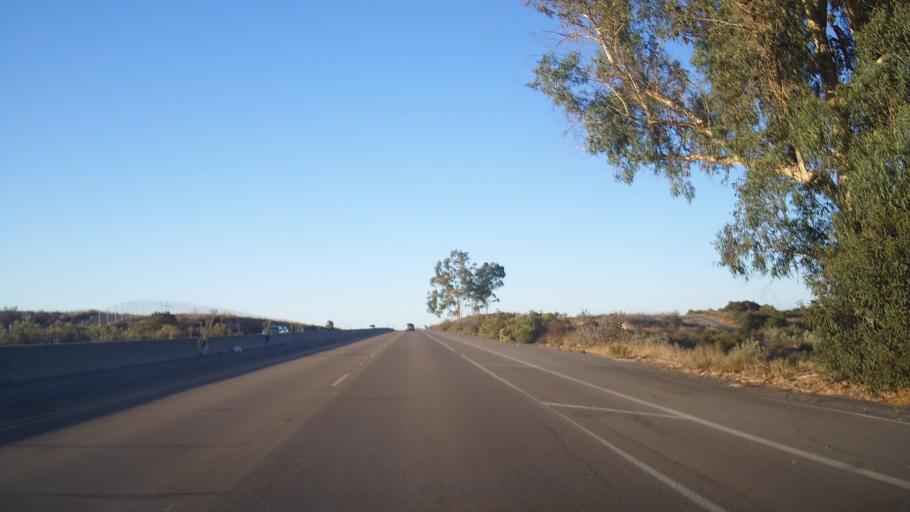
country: US
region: California
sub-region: San Diego County
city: Poway
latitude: 32.8697
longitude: -117.1165
